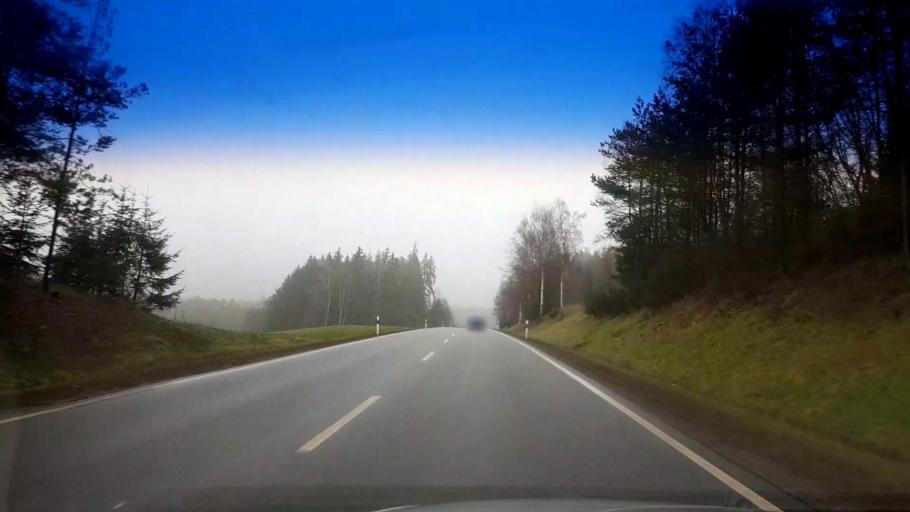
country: DE
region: Bavaria
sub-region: Upper Palatinate
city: Tirschenreuth
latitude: 49.8663
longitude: 12.2617
